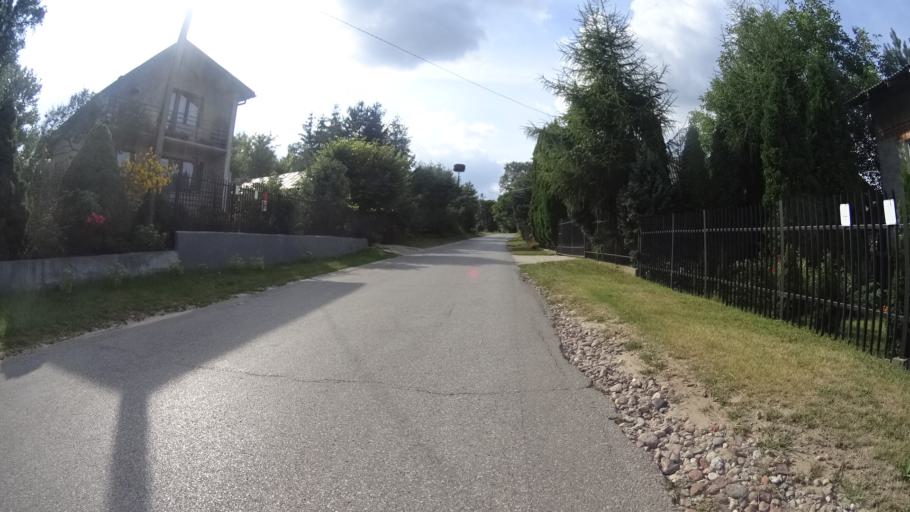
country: PL
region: Masovian Voivodeship
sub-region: Powiat grojecki
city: Mogielnica
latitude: 51.6547
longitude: 20.7639
